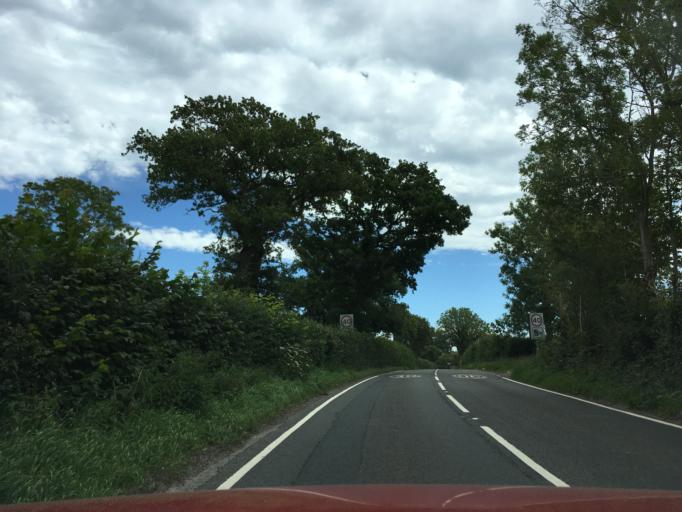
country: GB
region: England
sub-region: Somerset
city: Bradley Cross
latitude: 51.2689
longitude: -2.7697
